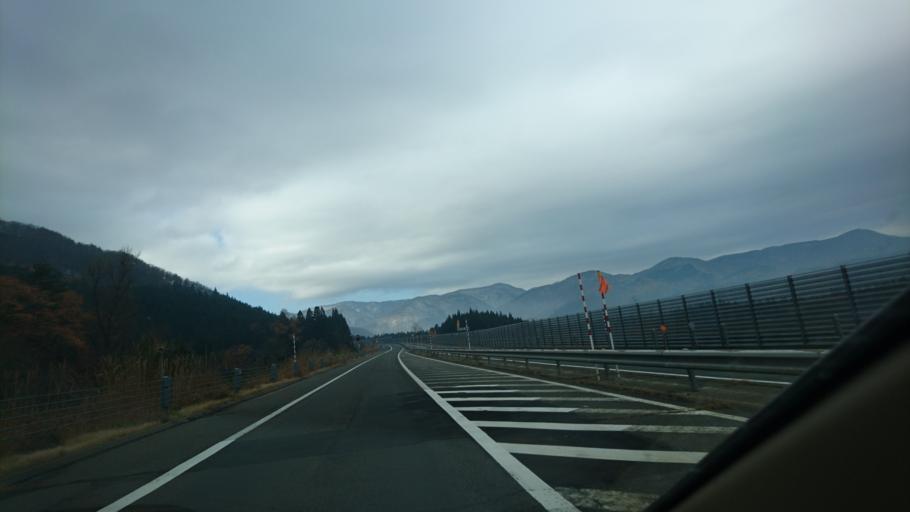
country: JP
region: Iwate
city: Kitakami
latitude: 39.2957
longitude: 140.9444
